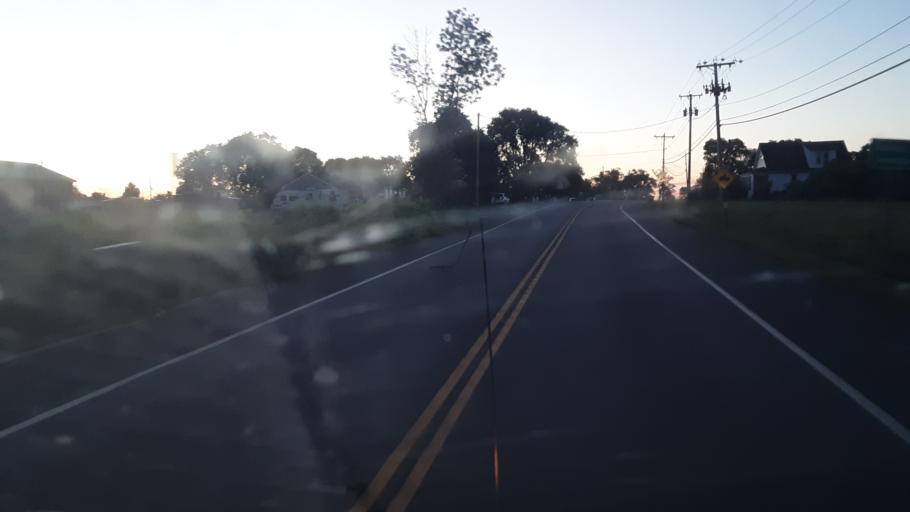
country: US
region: New York
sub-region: Montgomery County
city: Hagaman
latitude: 42.9471
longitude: -74.1440
